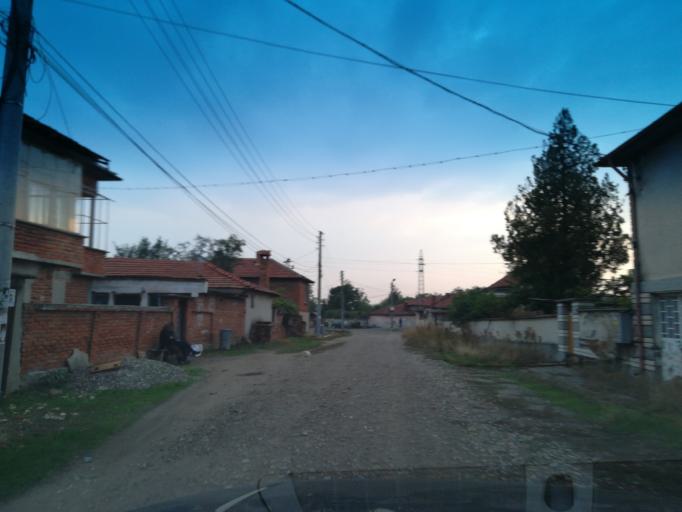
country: BG
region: Stara Zagora
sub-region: Obshtina Chirpan
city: Chirpan
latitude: 42.1727
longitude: 25.2067
